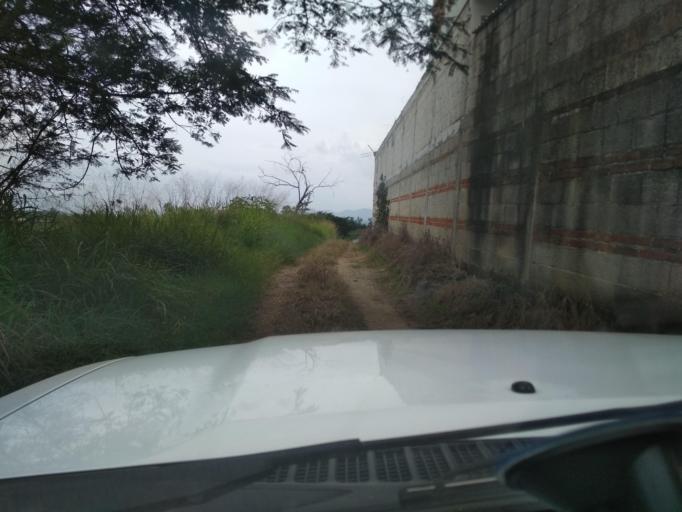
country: MX
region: Veracruz
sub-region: Emiliano Zapata
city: Dos Rios
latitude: 19.5304
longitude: -96.8091
